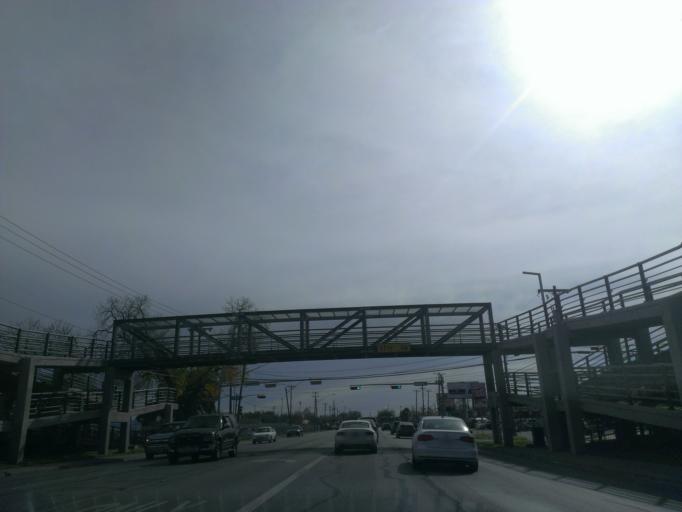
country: US
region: Texas
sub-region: Travis County
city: Austin
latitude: 30.2687
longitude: -97.6965
